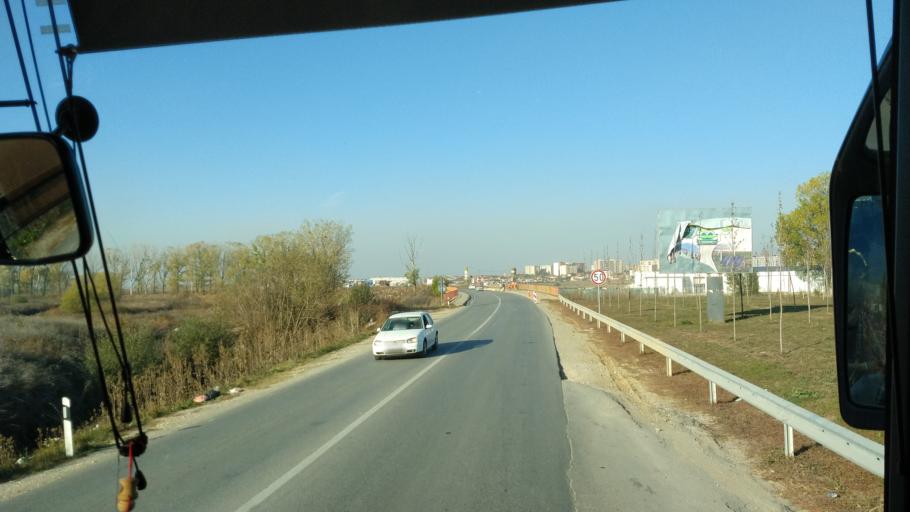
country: XK
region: Pristina
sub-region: Lipjan
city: Lipljan
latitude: 42.5120
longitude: 21.1129
